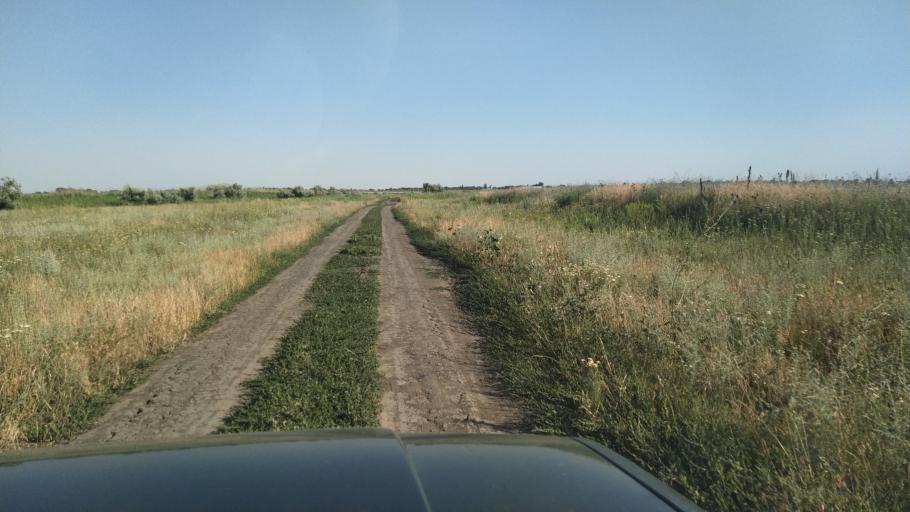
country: RU
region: Rostov
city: Kuleshovka
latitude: 47.1265
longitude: 39.6463
